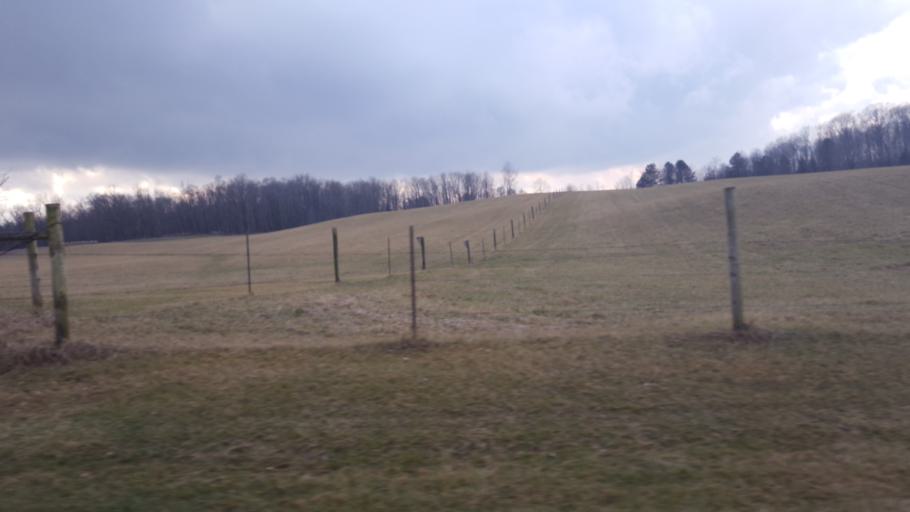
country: US
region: Ohio
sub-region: Morrow County
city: Mount Gilead
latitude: 40.5144
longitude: -82.6872
